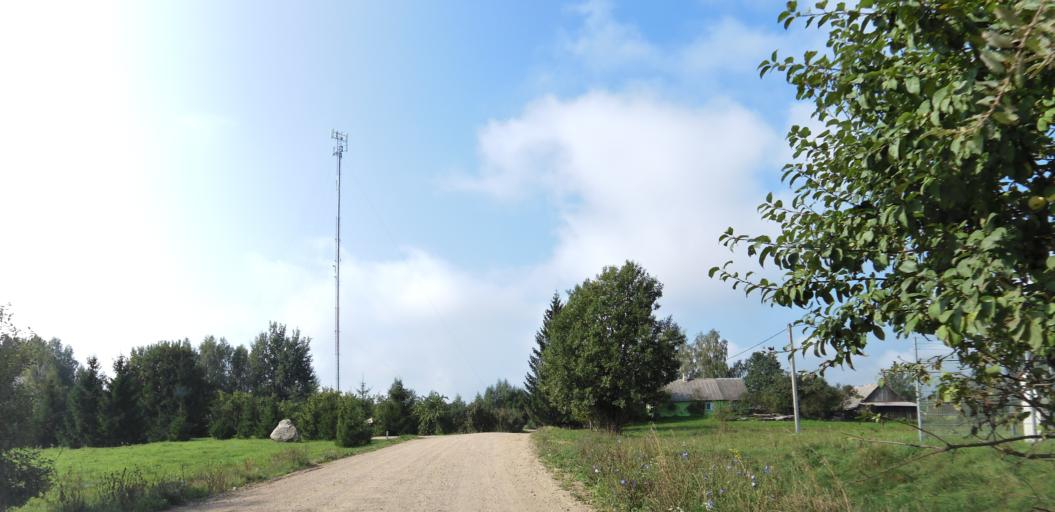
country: LT
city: Grigiskes
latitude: 54.7714
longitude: 25.0746
